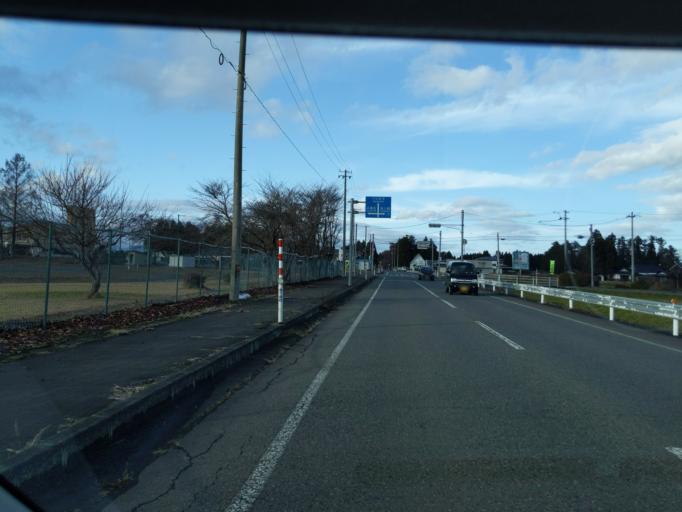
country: JP
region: Iwate
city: Mizusawa
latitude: 39.1961
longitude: 141.0693
